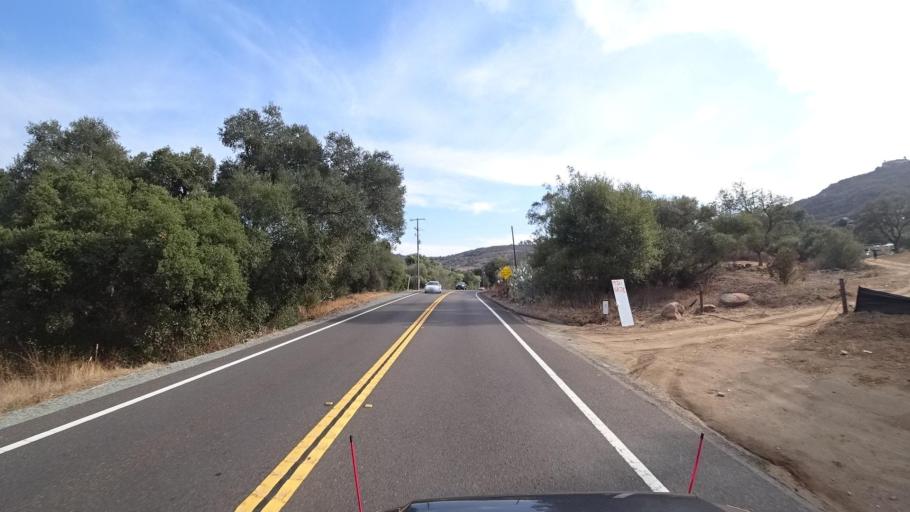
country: US
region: California
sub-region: San Diego County
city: Ramona
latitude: 33.0764
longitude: -116.9031
